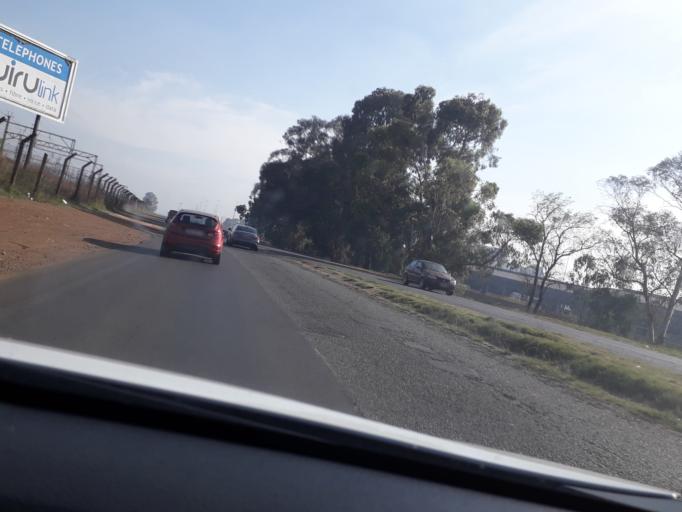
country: ZA
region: Gauteng
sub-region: Ekurhuleni Metropolitan Municipality
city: Boksburg
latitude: -26.1474
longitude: 28.2179
